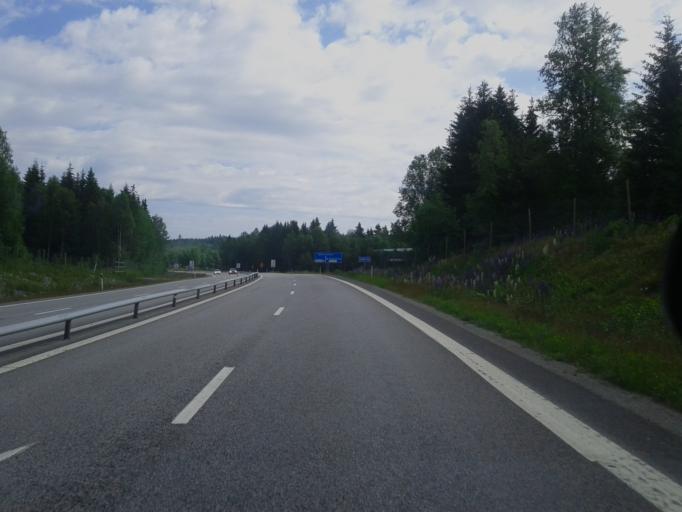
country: SE
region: Vaesternorrland
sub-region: OErnskoeldsviks Kommun
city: Ornskoldsvik
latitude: 63.2959
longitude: 18.8769
